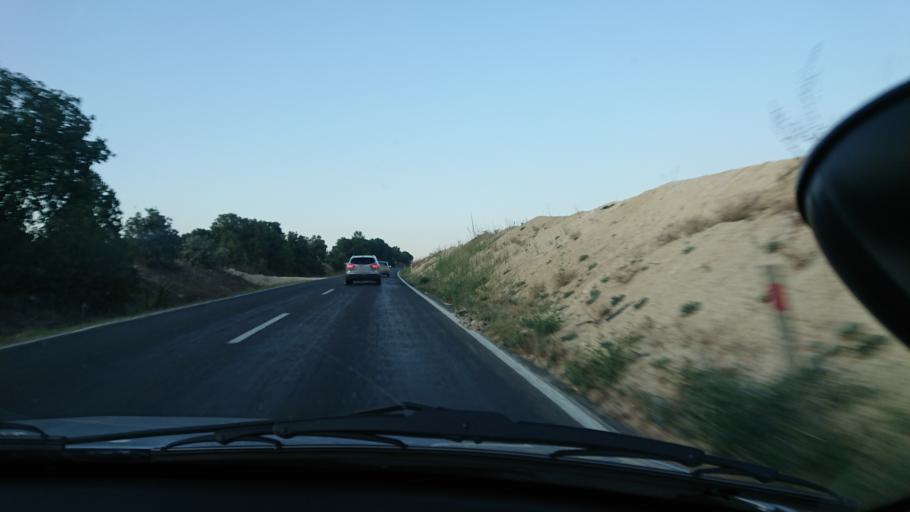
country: TR
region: Usak
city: Gure
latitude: 38.7599
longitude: 29.1989
